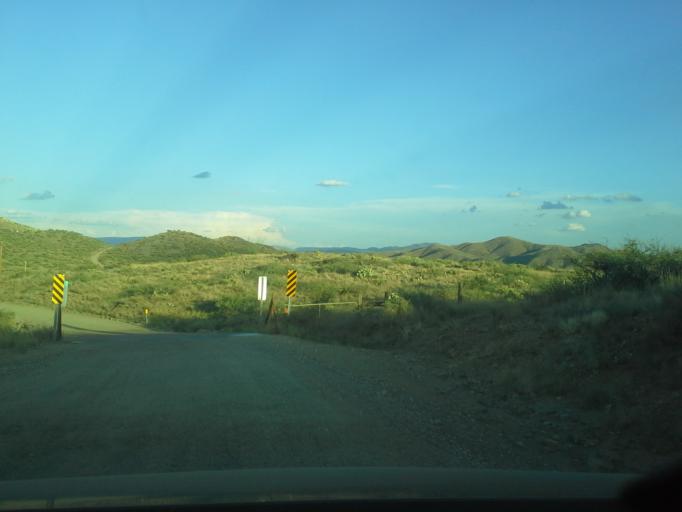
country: US
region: Arizona
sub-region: Yavapai County
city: Spring Valley
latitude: 34.2774
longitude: -112.2285
